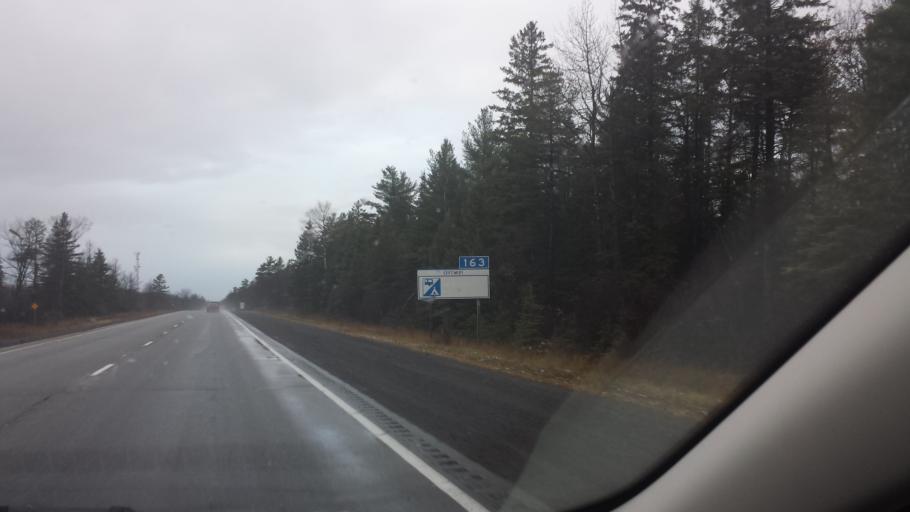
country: CA
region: Ontario
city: Carleton Place
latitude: 45.3277
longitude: -76.1336
